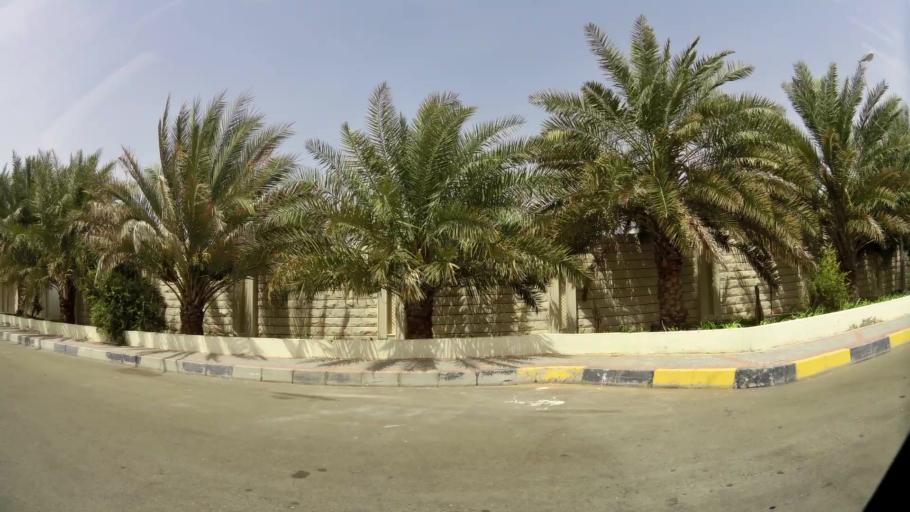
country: AE
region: Abu Dhabi
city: Al Ain
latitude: 24.1430
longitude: 55.6418
